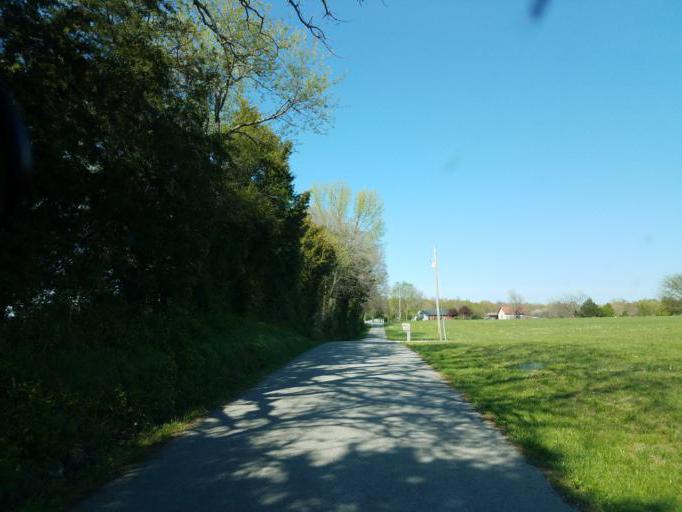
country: US
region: Kentucky
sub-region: Edmonson County
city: Brownsville
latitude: 37.1245
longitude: -86.1496
